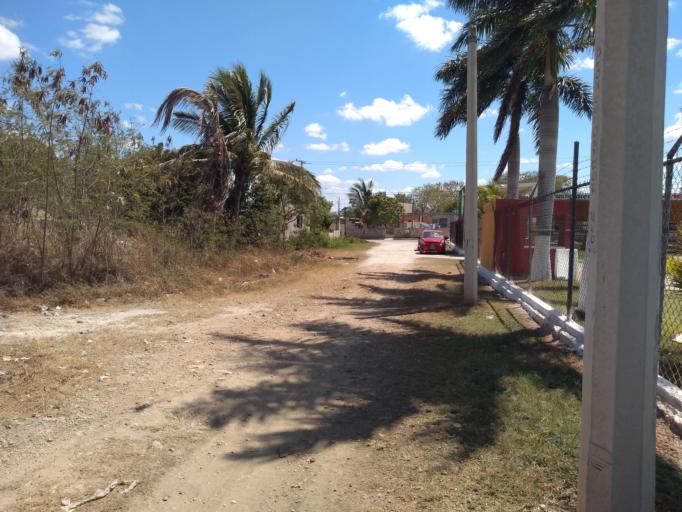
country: MX
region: Yucatan
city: Itzincab Palomeque
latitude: 20.9250
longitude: -89.6668
